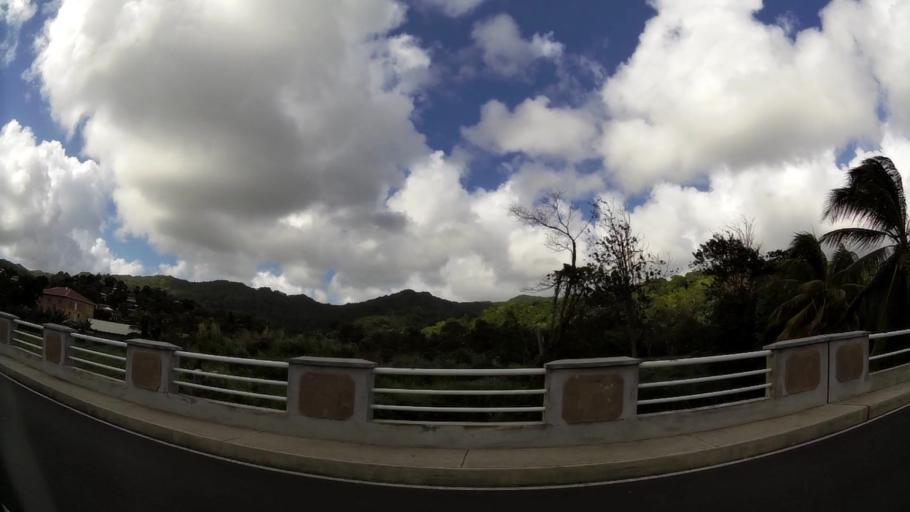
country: LC
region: Dennery Quarter
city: Dennery
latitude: 13.9320
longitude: -60.9309
